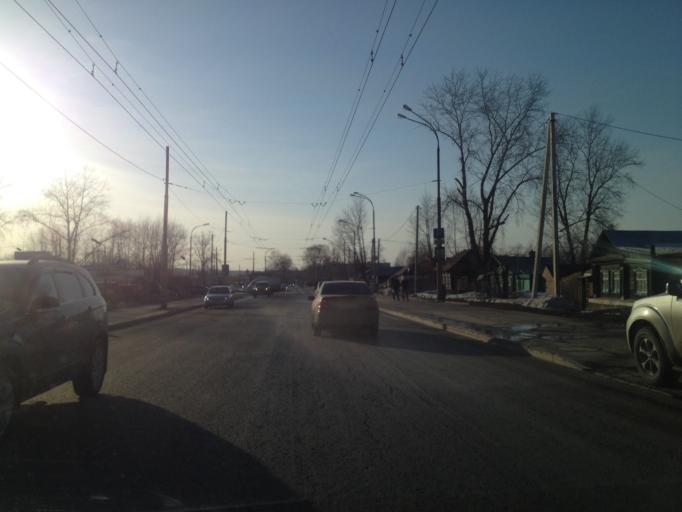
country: RU
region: Sverdlovsk
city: Shirokaya Rechka
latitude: 56.8319
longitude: 60.5344
